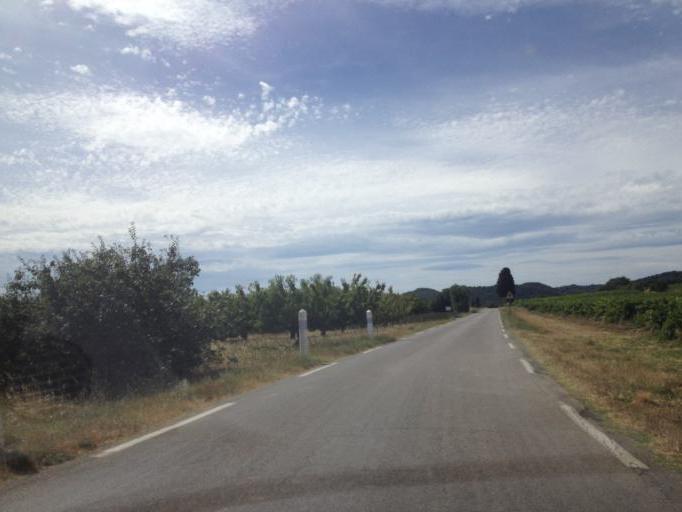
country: FR
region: Provence-Alpes-Cote d'Azur
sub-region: Departement du Vaucluse
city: Caromb
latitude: 44.1194
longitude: 5.0658
